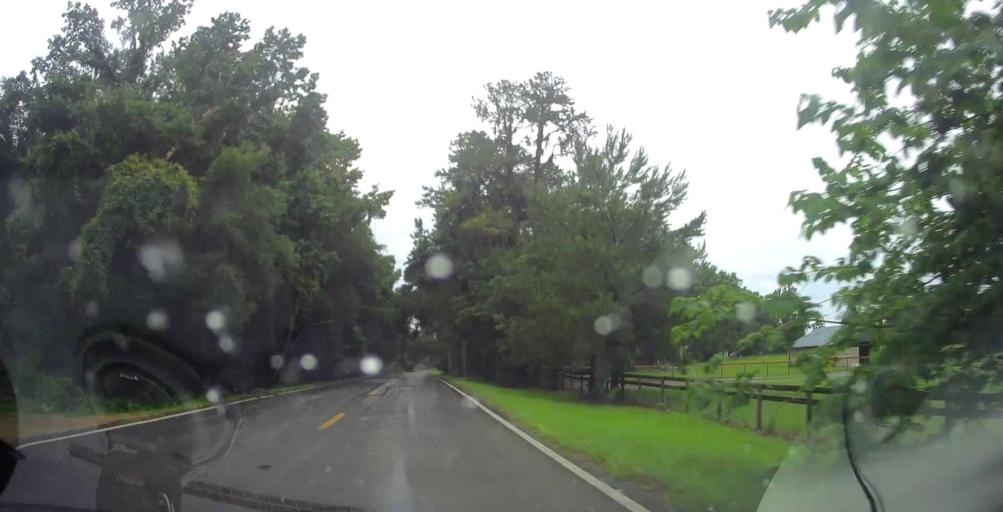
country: US
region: Florida
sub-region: Marion County
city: Citra
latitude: 29.3413
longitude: -82.2130
